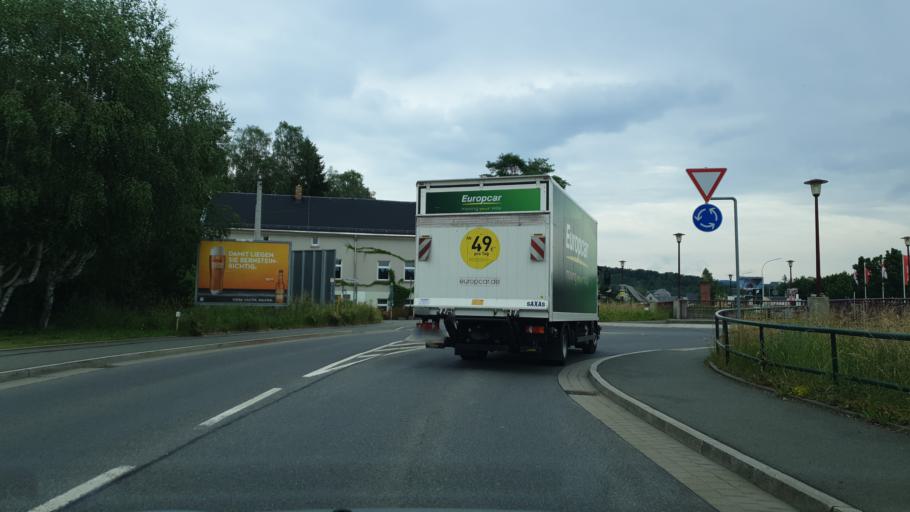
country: DE
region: Saxony
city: Rodewisch
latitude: 50.5417
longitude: 12.3949
